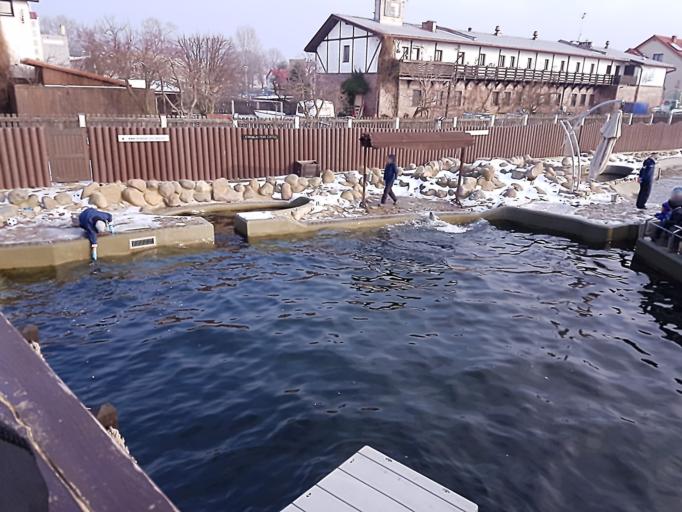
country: PL
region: Pomeranian Voivodeship
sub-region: Powiat pucki
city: Hel
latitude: 54.6069
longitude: 18.7999
